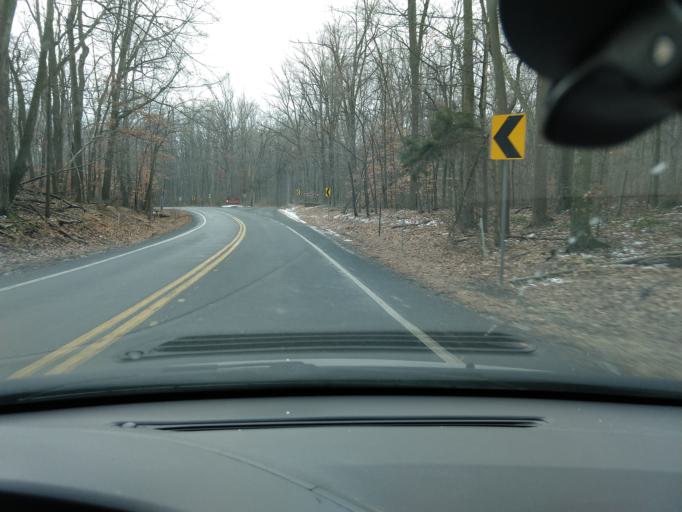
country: US
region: Pennsylvania
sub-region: Berks County
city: Birdsboro
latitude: 40.2149
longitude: -75.7751
